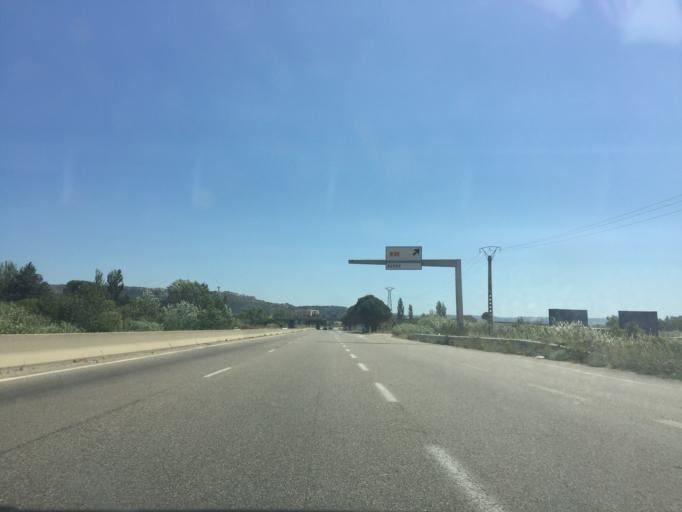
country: FR
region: Provence-Alpes-Cote d'Azur
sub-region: Departement des Bouches-du-Rhone
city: Rognac
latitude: 43.4961
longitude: 5.2156
